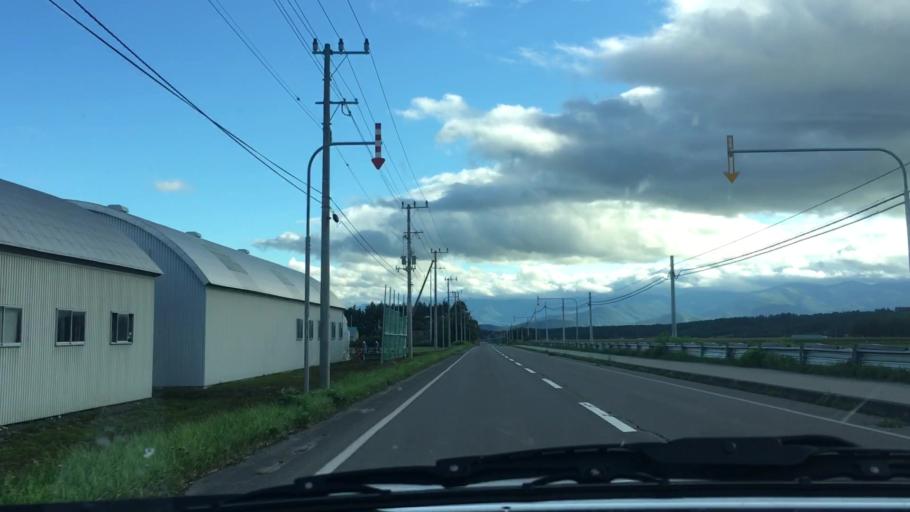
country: JP
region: Hokkaido
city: Otofuke
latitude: 43.1471
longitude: 142.8986
